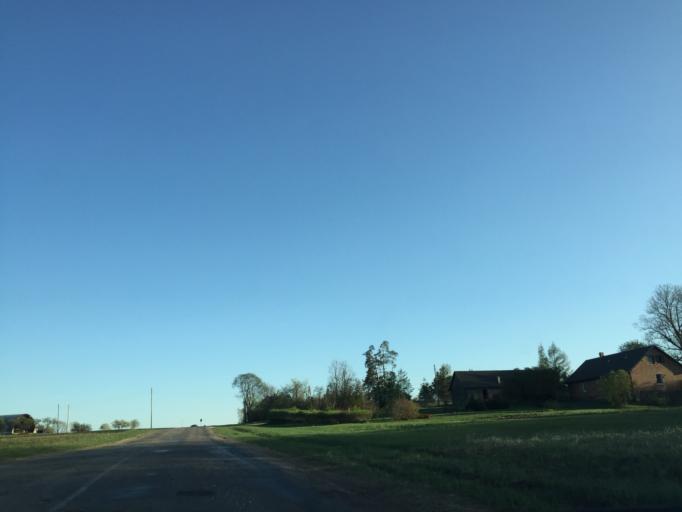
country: LV
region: Koknese
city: Koknese
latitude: 56.7115
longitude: 25.4934
